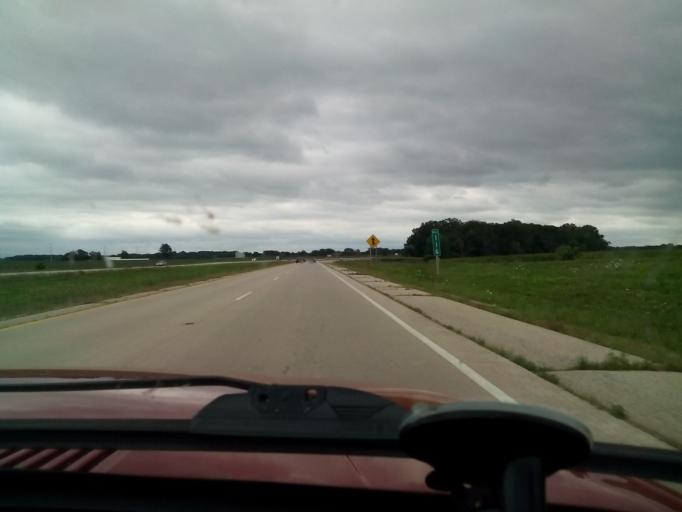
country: US
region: Wisconsin
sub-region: Columbia County
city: Columbus
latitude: 43.3149
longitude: -89.0458
